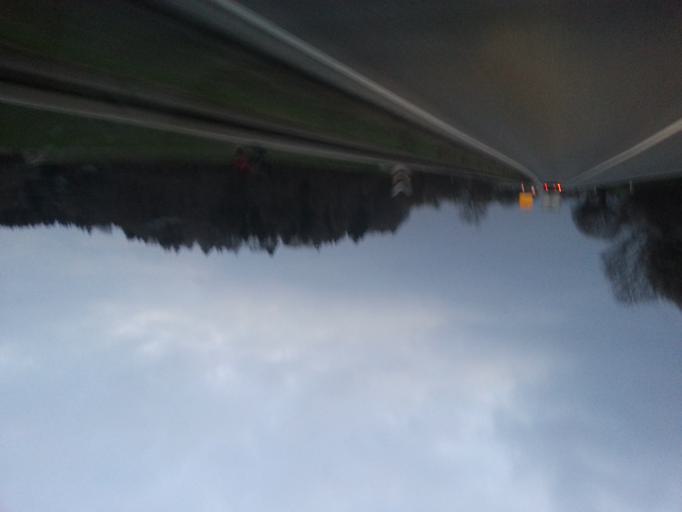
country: DE
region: Baden-Wuerttemberg
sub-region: Tuebingen Region
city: Bad Waldsee
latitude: 47.9081
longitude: 9.7377
